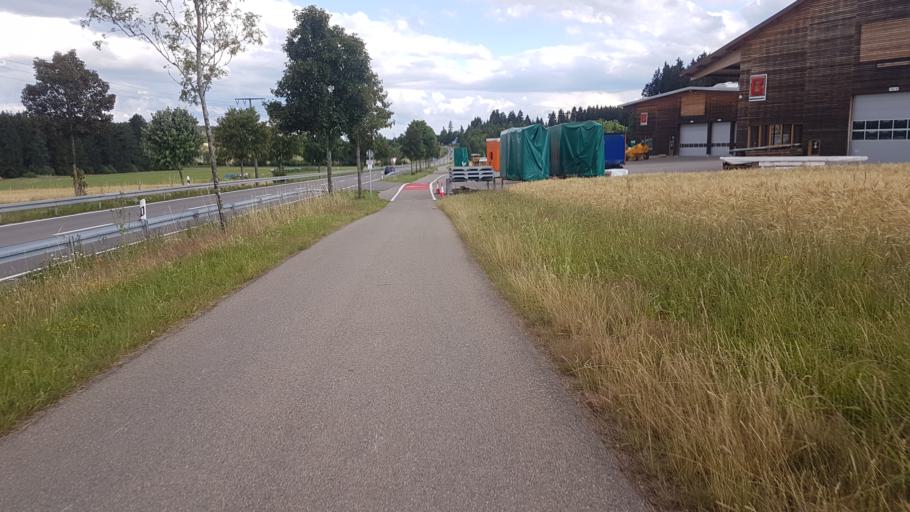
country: DE
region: Baden-Wuerttemberg
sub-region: Freiburg Region
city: Unterkirnach
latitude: 48.0136
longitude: 8.4077
